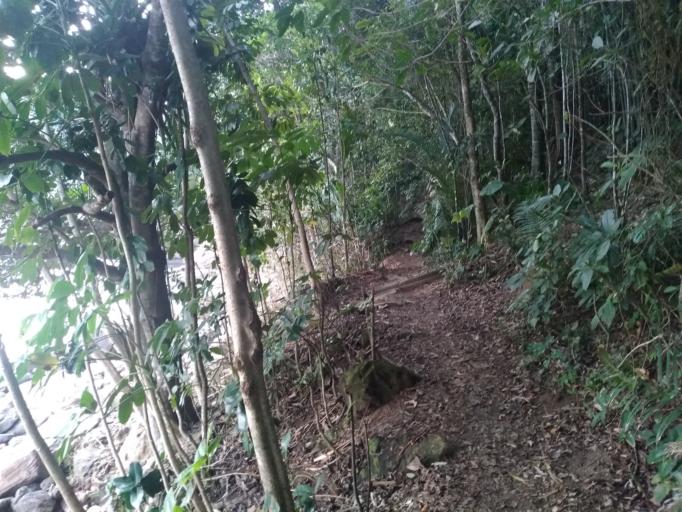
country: BR
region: Sao Paulo
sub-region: Ubatuba
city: Ubatuba
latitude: -23.4921
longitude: -45.1031
